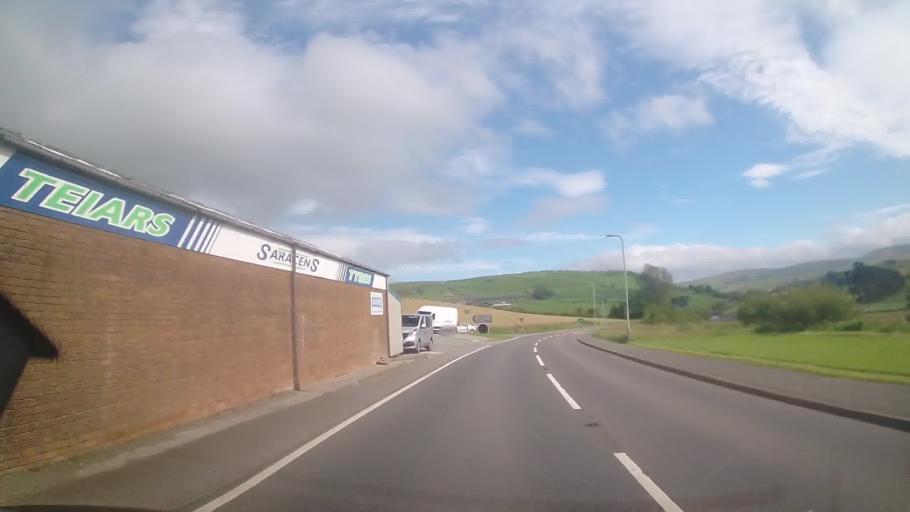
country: GB
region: Wales
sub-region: Conwy
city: Llangwm
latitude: 53.0230
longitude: -3.5611
